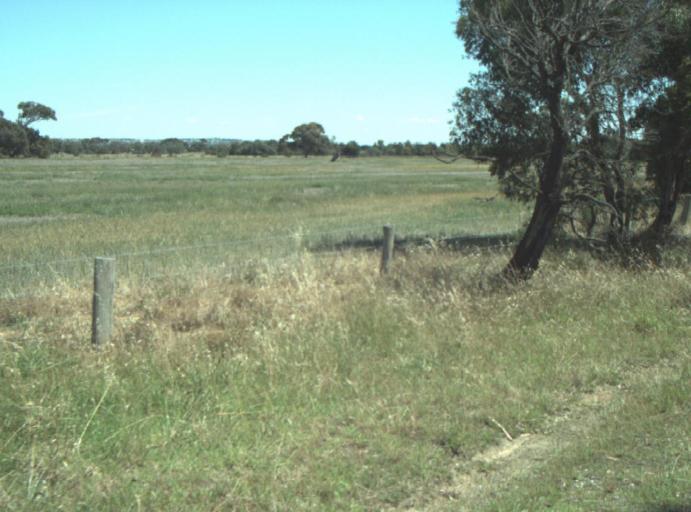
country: AU
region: Victoria
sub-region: Greater Geelong
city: Breakwater
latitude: -38.2134
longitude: 144.3580
